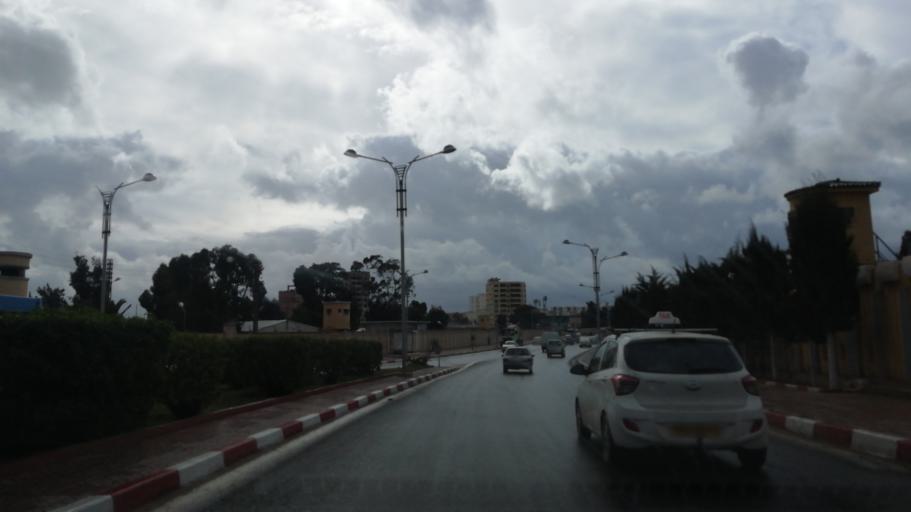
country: DZ
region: Oran
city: Oran
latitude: 35.6829
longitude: -0.6712
